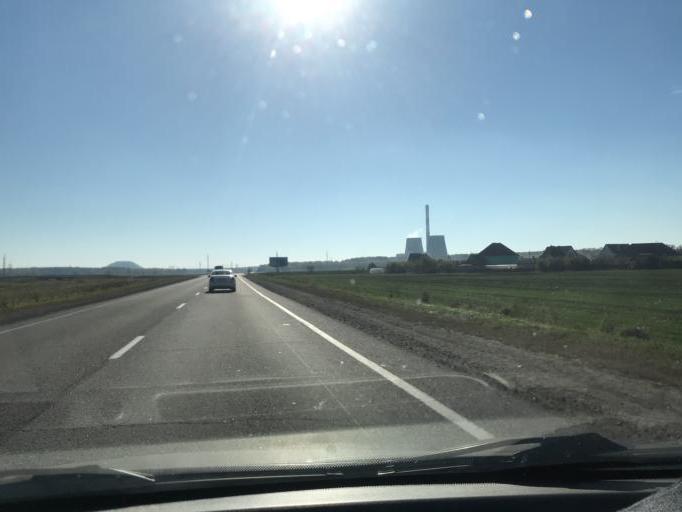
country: BY
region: Gomel
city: Kastsyukowka
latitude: 52.4655
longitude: 30.8243
